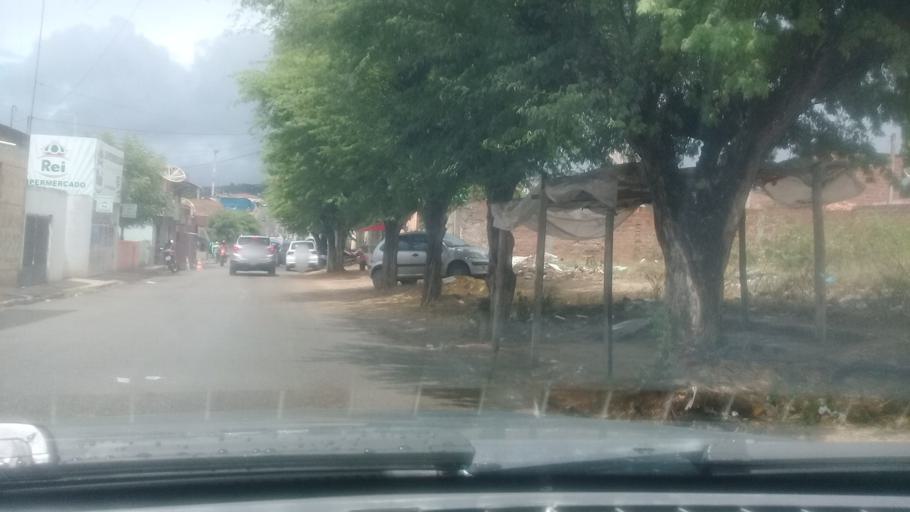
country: BR
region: Pernambuco
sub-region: Vitoria De Santo Antao
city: Vitoria de Santo Antao
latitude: -8.1242
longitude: -35.2918
